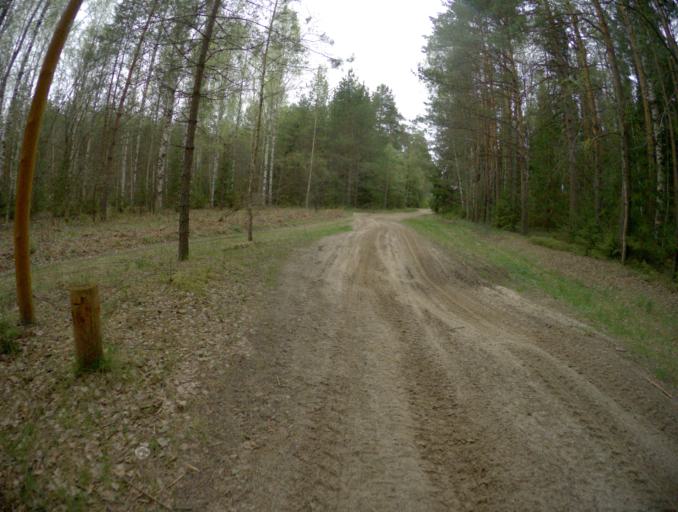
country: RU
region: Vladimir
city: Golovino
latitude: 55.9026
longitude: 40.4391
